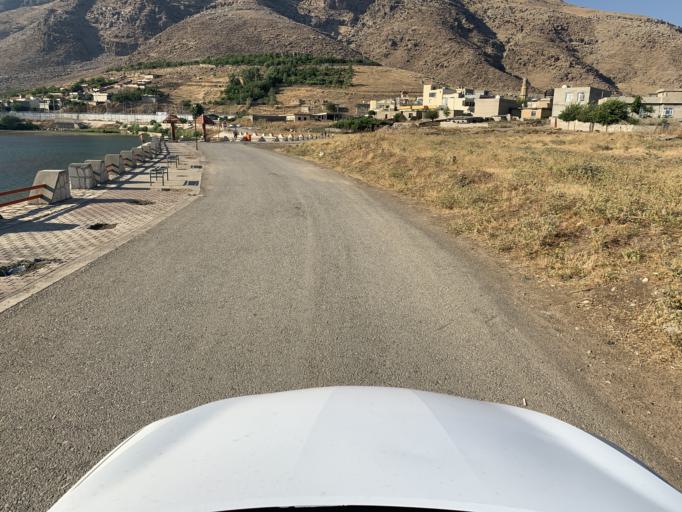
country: IQ
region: As Sulaymaniyah
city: Raniye
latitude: 36.2725
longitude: 44.7557
